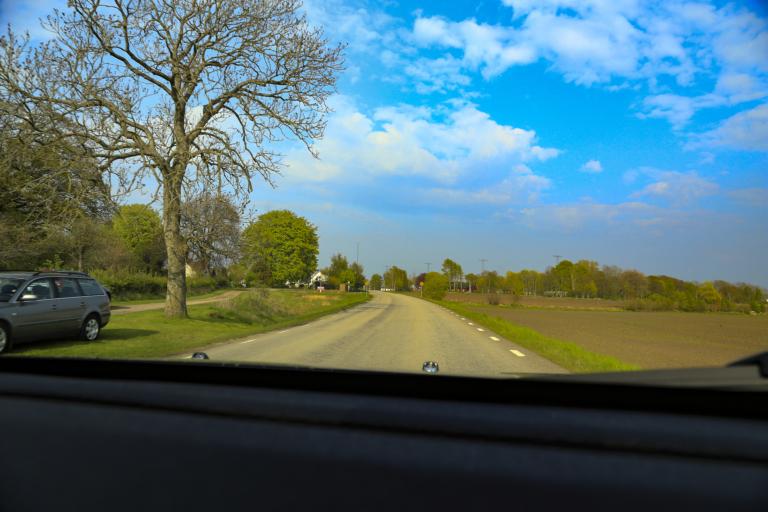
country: SE
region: Halland
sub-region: Varbergs Kommun
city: Tvaaker
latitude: 57.1001
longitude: 12.3519
